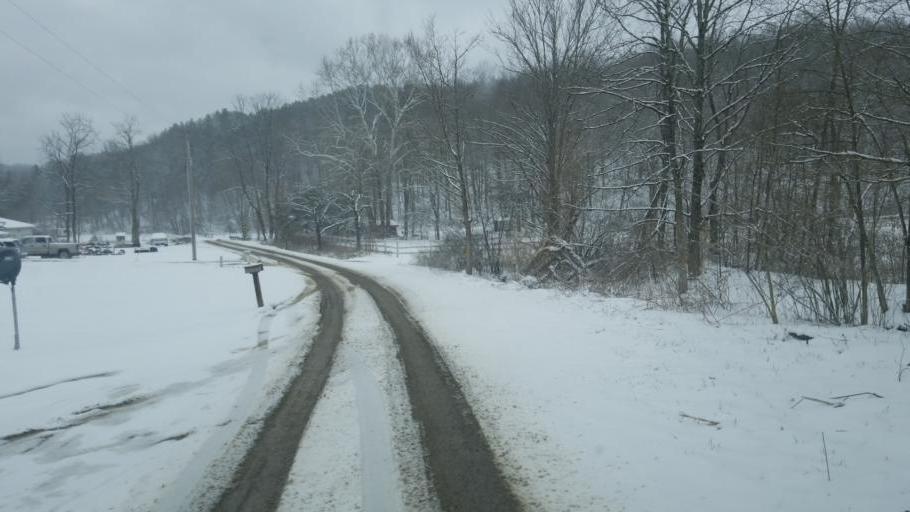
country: US
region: Ohio
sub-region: Knox County
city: Oak Hill
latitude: 40.4510
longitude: -82.1699
